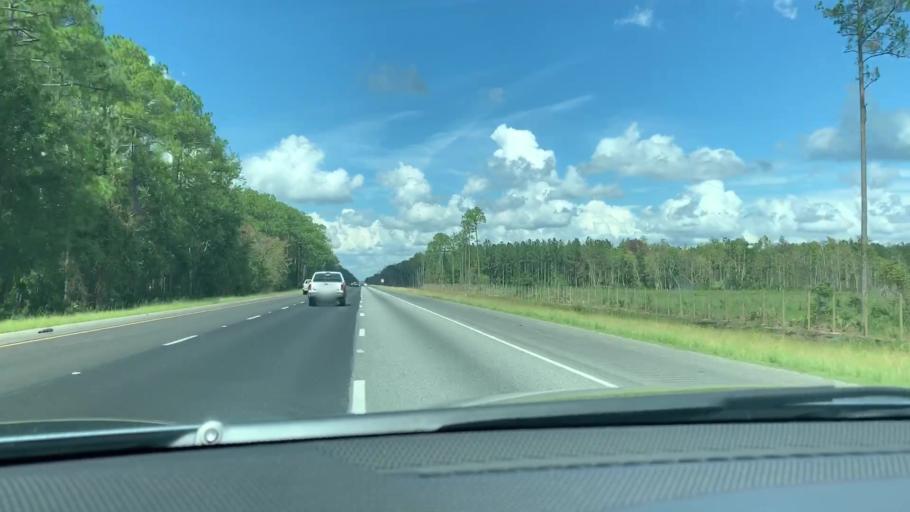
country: US
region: Georgia
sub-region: Camden County
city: Kingsland
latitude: 30.8822
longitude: -81.6857
